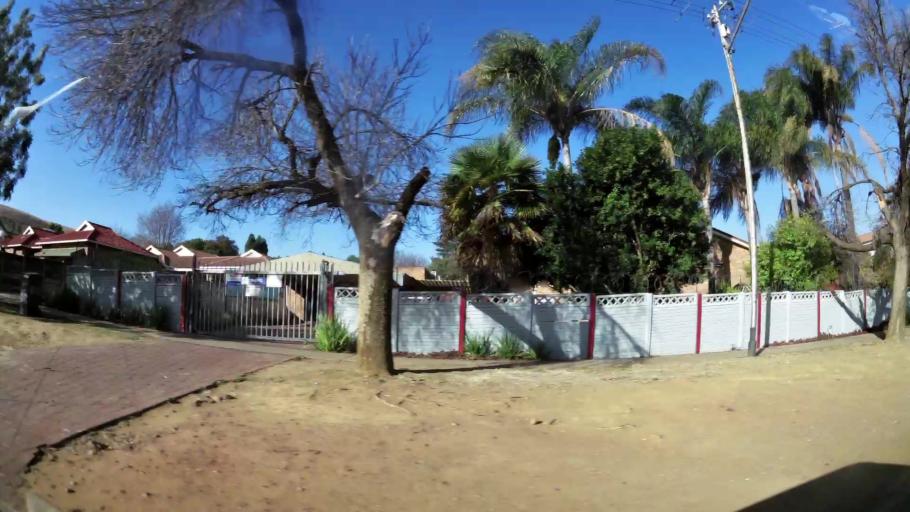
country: ZA
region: Gauteng
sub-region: City of Tshwane Metropolitan Municipality
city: Pretoria
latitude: -25.6994
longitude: 28.2428
